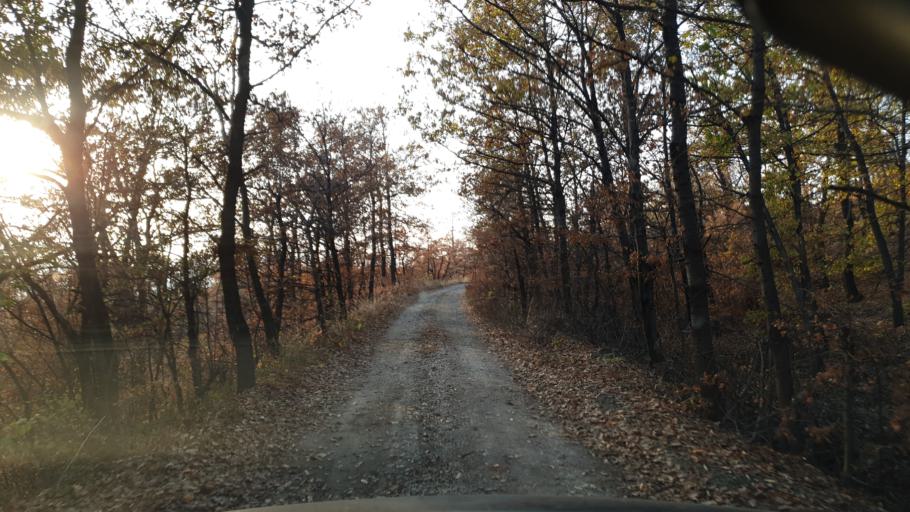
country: RS
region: Central Serbia
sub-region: Borski Okrug
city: Bor
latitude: 44.0683
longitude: 22.0763
